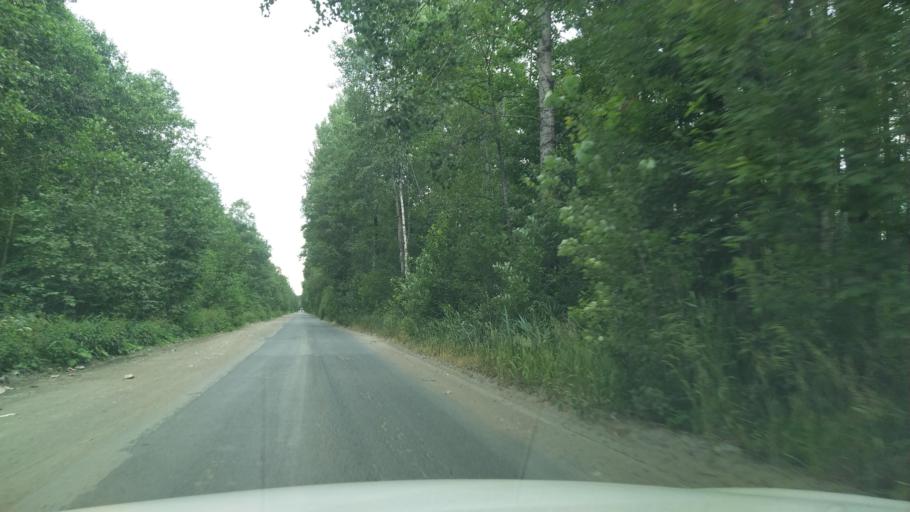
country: RU
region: St.-Petersburg
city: Bol'shaya Izhora
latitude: 59.9162
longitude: 29.5744
